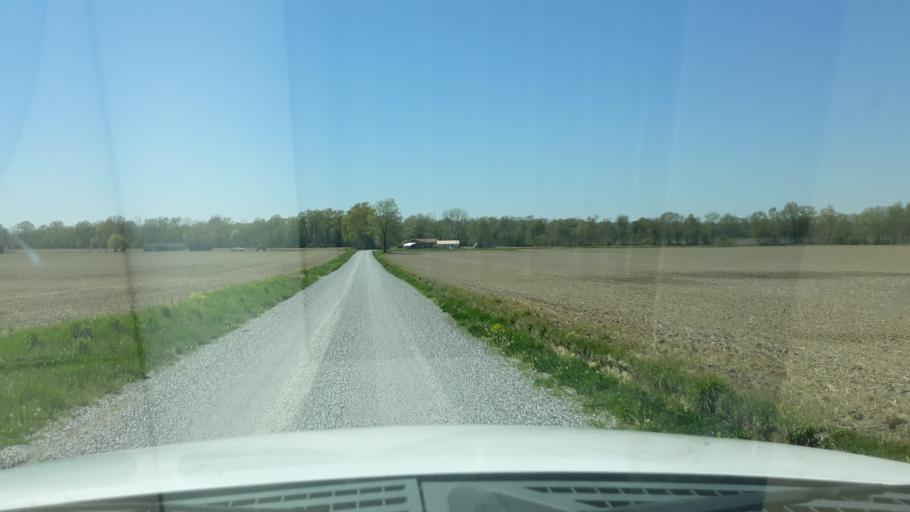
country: US
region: Illinois
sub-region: Saline County
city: Harrisburg
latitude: 37.8923
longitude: -88.6747
